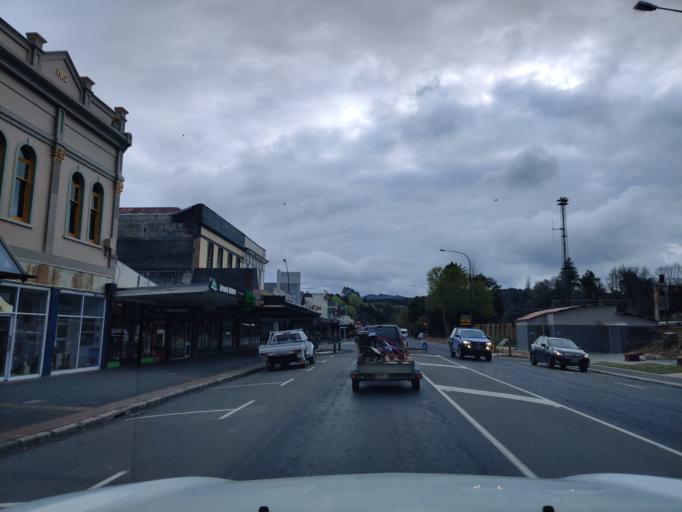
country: NZ
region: Waikato
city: Turangi
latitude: -38.8831
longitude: 175.2636
